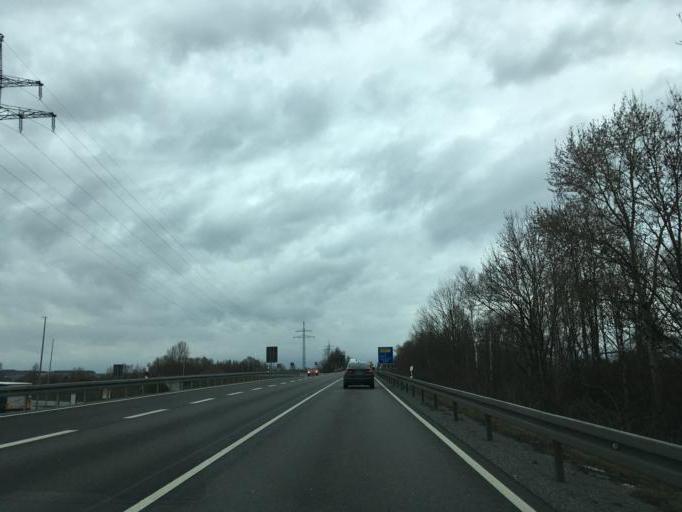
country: DE
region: Bavaria
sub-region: Lower Bavaria
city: Pilsting
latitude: 48.6925
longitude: 12.6747
